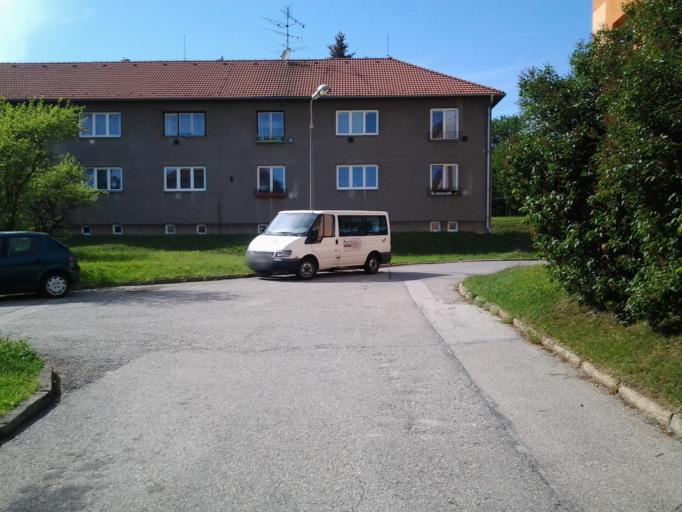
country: CZ
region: Jihocesky
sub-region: Okres Cesky Krumlov
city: Cesky Krumlov
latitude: 48.8217
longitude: 14.3106
